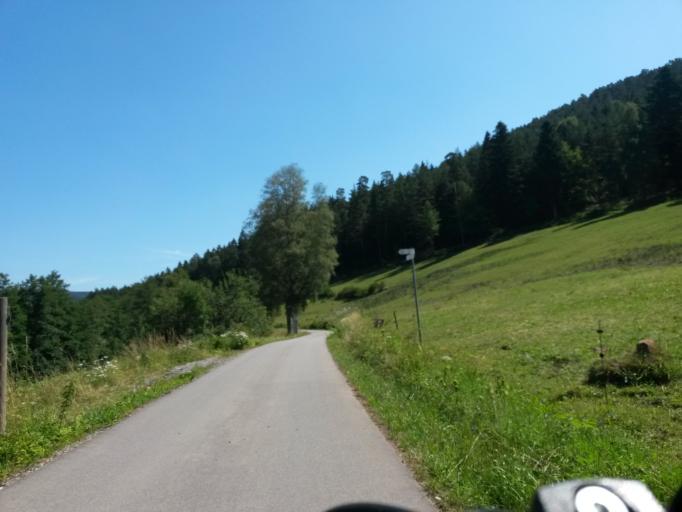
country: DE
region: Baden-Wuerttemberg
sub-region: Karlsruhe Region
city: Enzklosterle
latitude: 48.6770
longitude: 8.4810
